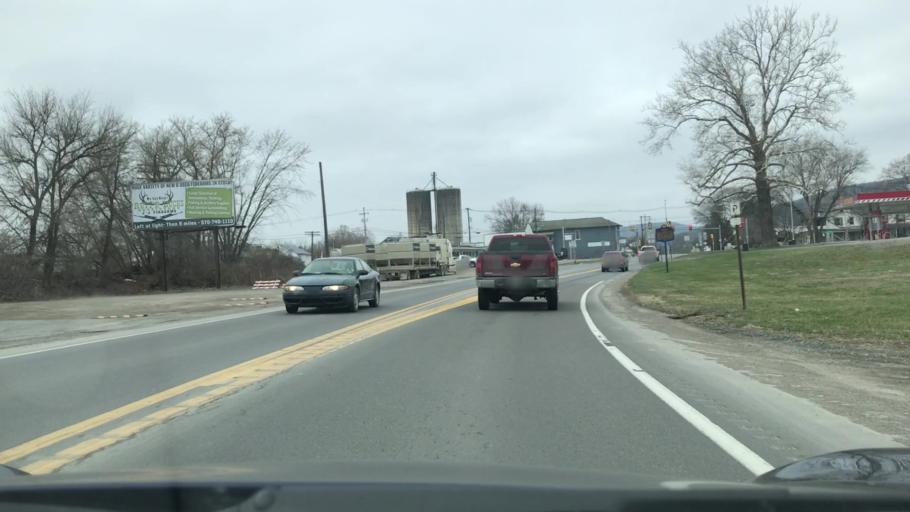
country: US
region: Pennsylvania
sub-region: Bradford County
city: Towanda
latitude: 41.7745
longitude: -76.3973
